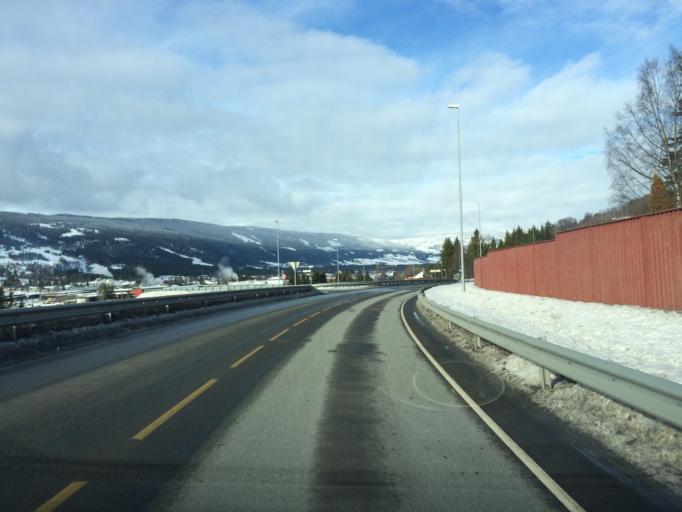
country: NO
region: Oppland
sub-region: Gausdal
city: Segalstad bru
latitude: 61.2232
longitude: 10.2342
